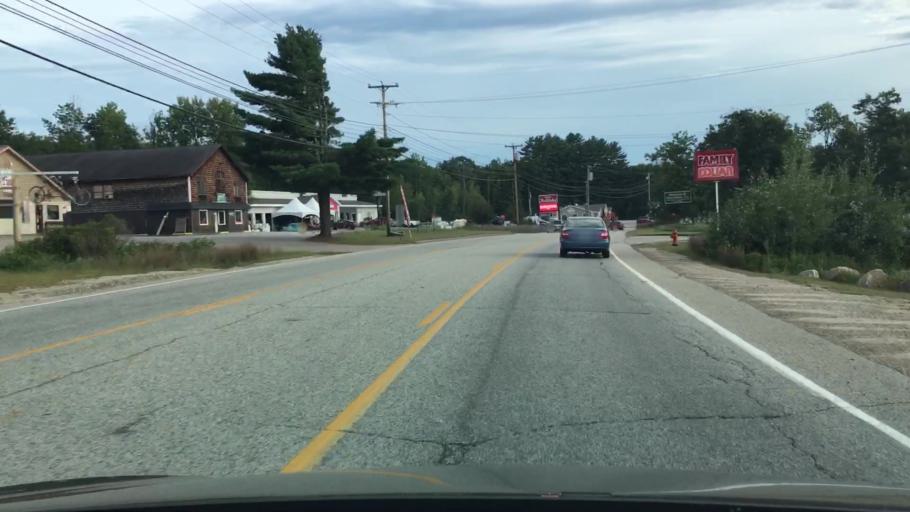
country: US
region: Maine
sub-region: Cumberland County
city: Bridgton
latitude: 44.0413
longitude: -70.6997
